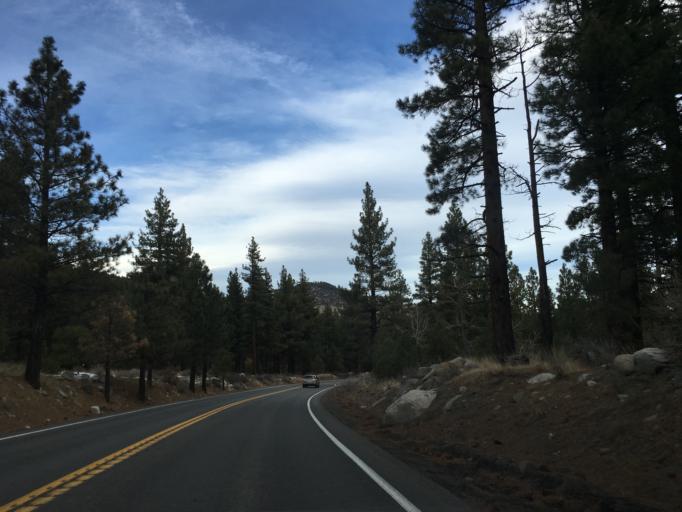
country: US
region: Nevada
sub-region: Washoe County
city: Incline Village
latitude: 39.3559
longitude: -119.8561
